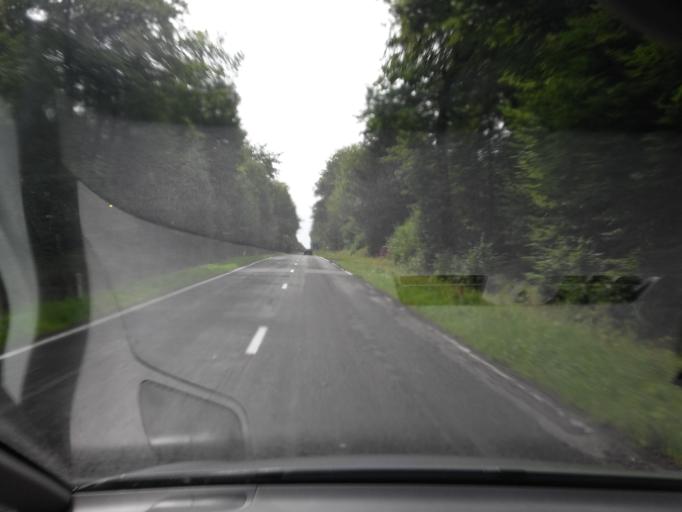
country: BE
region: Wallonia
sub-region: Province du Luxembourg
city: Chiny
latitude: 49.7663
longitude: 5.3632
